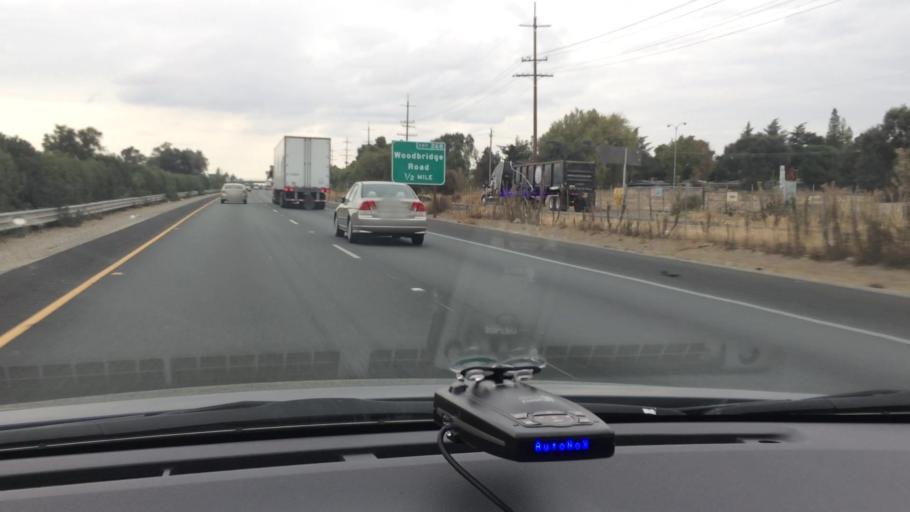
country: US
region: California
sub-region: San Joaquin County
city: Lodi
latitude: 38.1537
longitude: -121.2614
